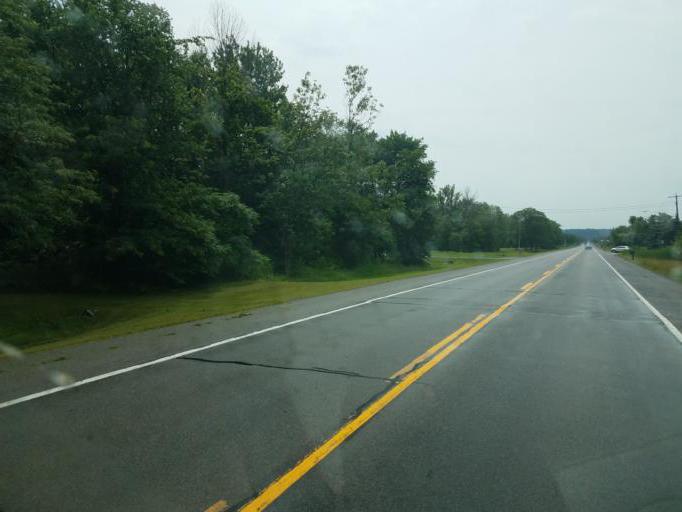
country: US
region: New York
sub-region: Niagara County
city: Lewiston
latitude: 43.2031
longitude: -79.0177
